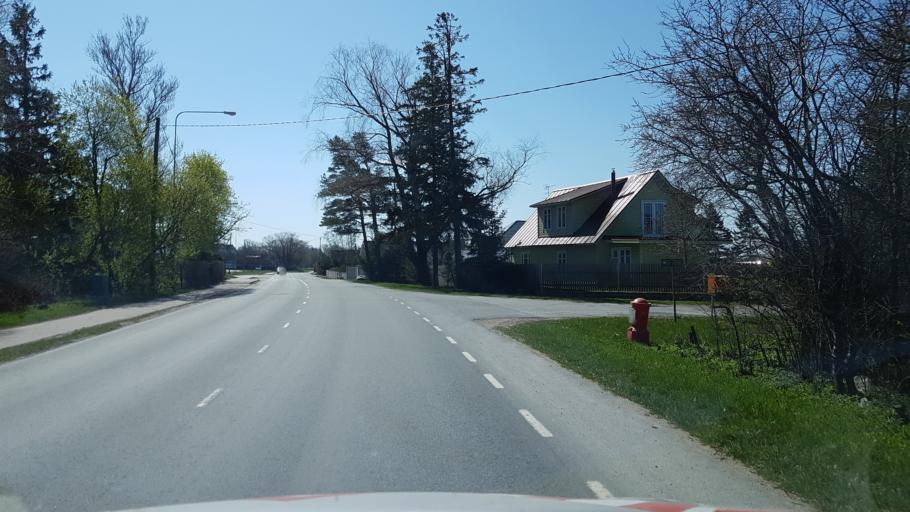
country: EE
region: Harju
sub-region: Viimsi vald
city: Rummu
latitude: 59.5401
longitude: 24.7941
